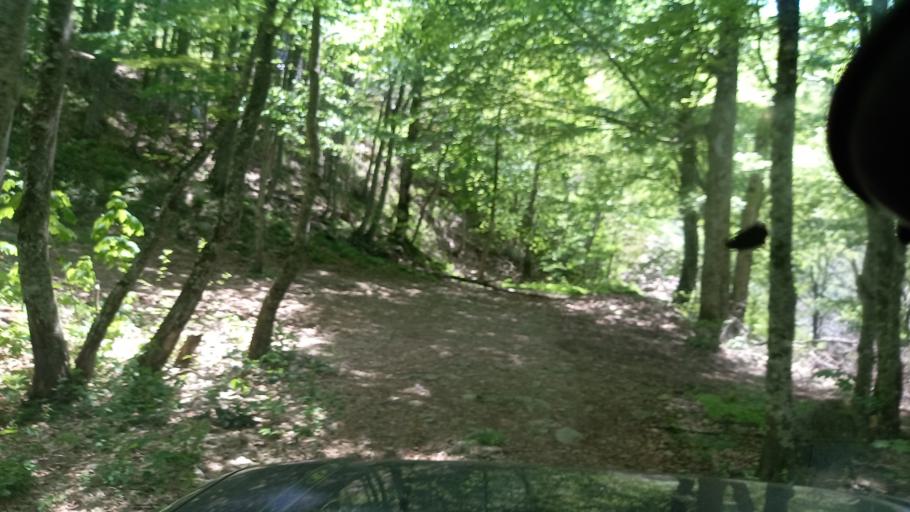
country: RU
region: Krasnodarskiy
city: Tuapse
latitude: 44.2489
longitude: 39.2803
